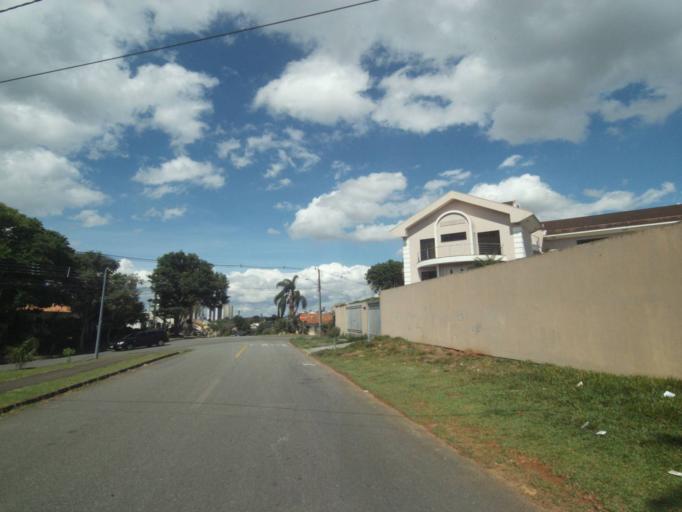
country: BR
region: Parana
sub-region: Curitiba
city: Curitiba
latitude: -25.4440
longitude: -49.3313
